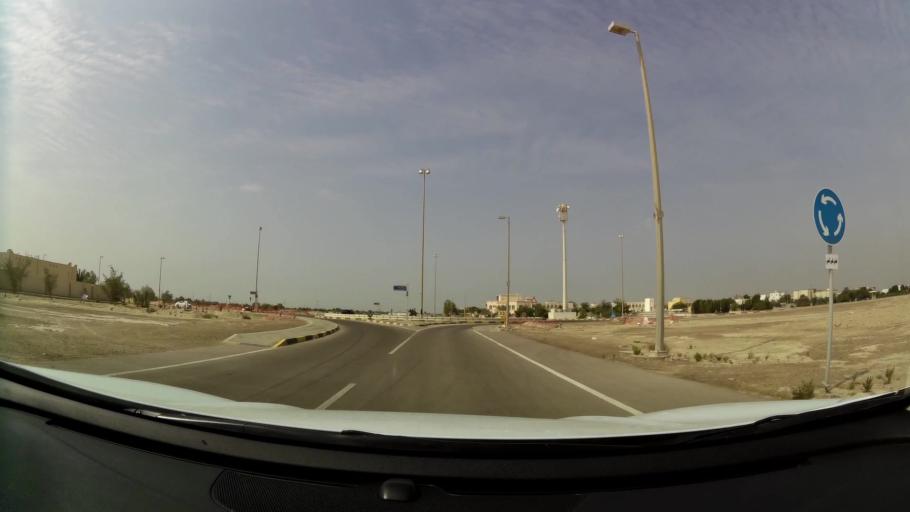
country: AE
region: Abu Dhabi
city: Abu Dhabi
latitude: 24.5372
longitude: 54.6726
